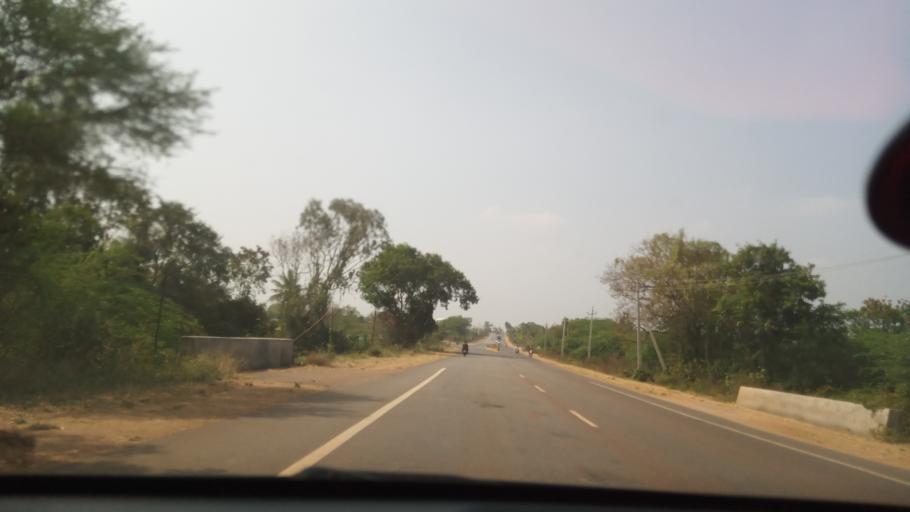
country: IN
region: Karnataka
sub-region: Mysore
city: Nanjangud
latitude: 12.0892
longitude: 76.7274
